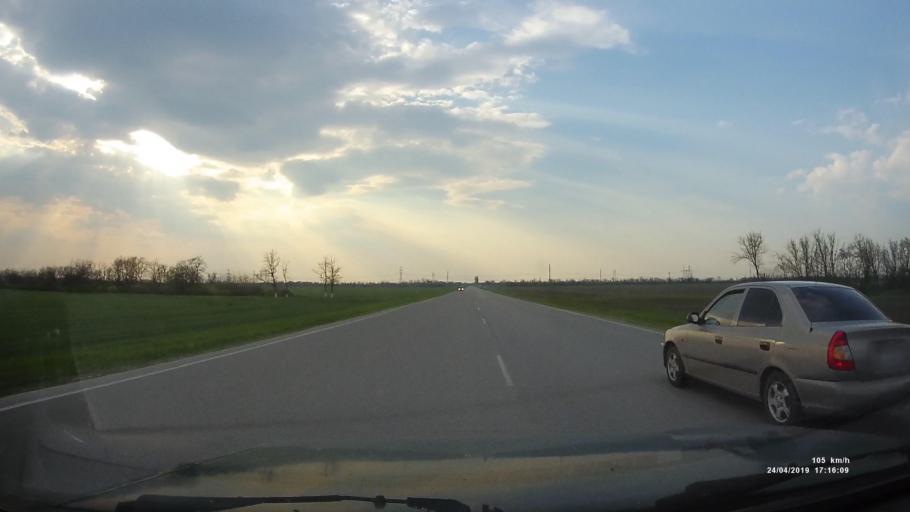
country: RU
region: Rostov
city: Gigant
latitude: 46.4964
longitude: 41.4308
